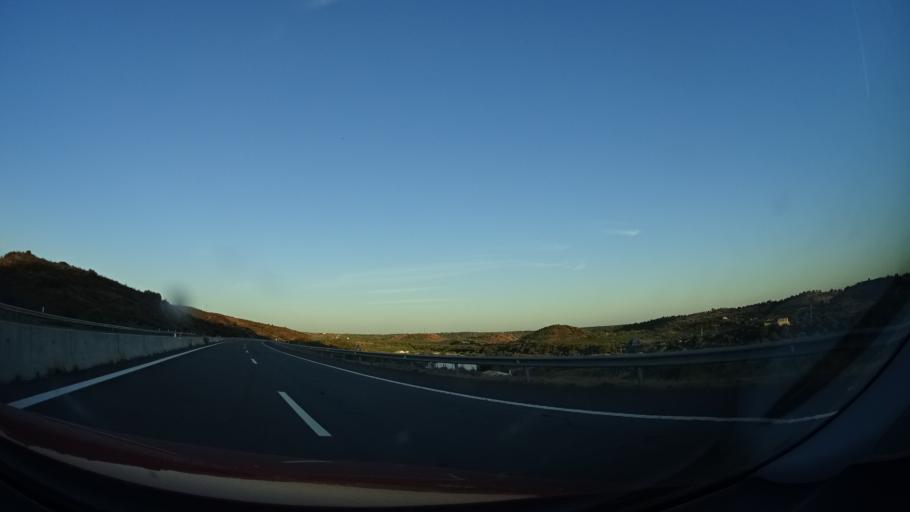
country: PT
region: Faro
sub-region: Tavira
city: Tavira
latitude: 37.1698
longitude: -7.6375
